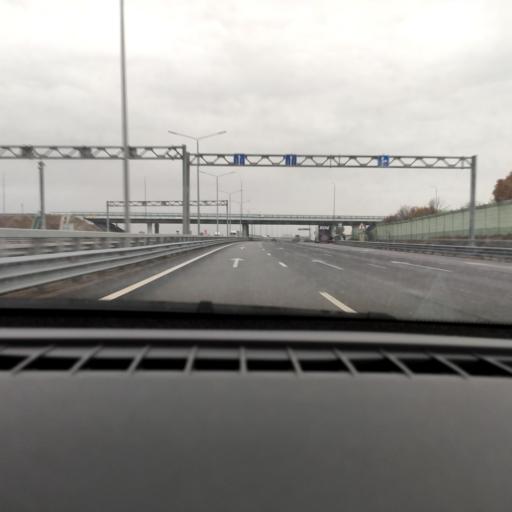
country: RU
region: Voronezj
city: Ramon'
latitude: 51.8240
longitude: 39.2498
